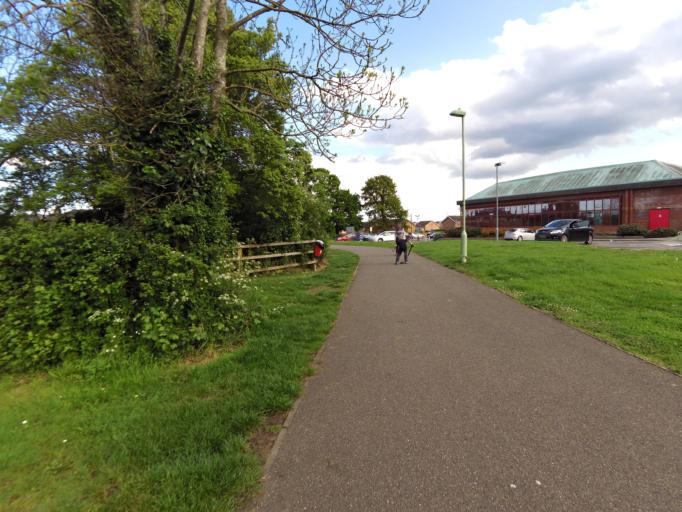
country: GB
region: England
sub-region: Suffolk
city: Stowmarket
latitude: 52.1933
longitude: 0.9807
